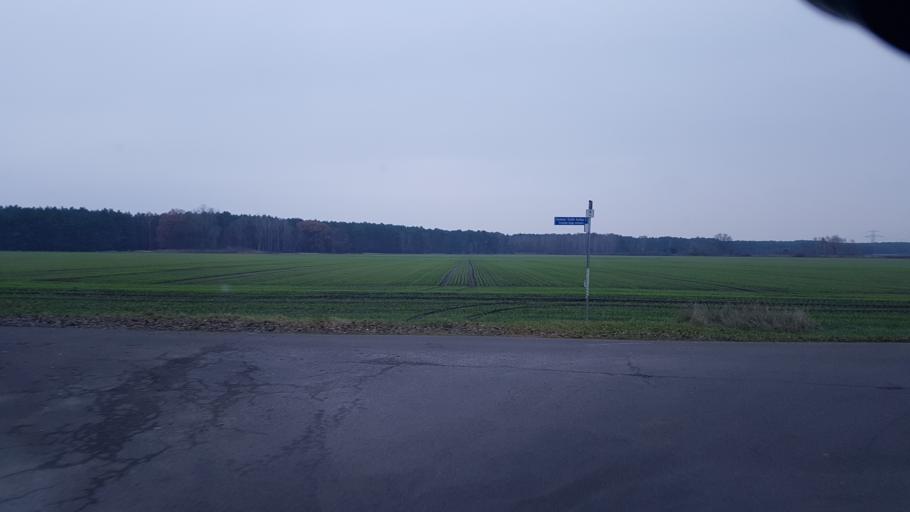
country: DE
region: Brandenburg
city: Peitz
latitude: 51.8854
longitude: 14.4019
